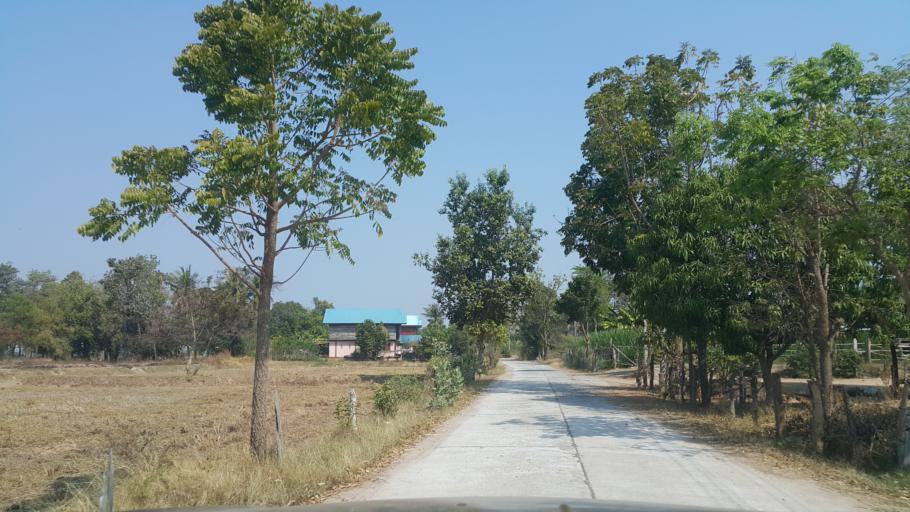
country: TH
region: Buriram
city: Krasang
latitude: 15.0961
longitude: 103.3715
